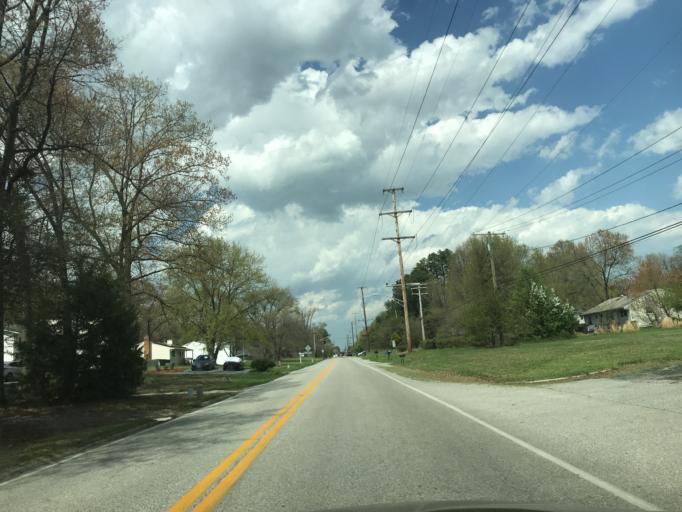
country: US
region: Maryland
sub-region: Anne Arundel County
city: Severn
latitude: 39.1170
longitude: -76.6818
